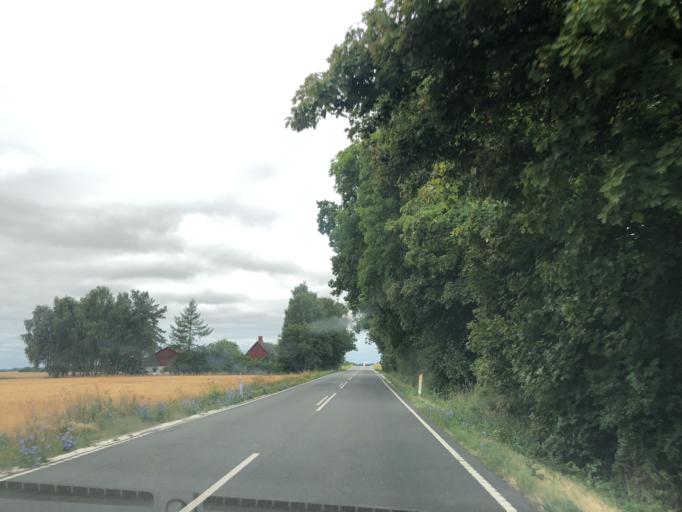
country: DK
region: Zealand
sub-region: Slagelse Kommune
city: Skaelskor
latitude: 55.2971
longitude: 11.3334
